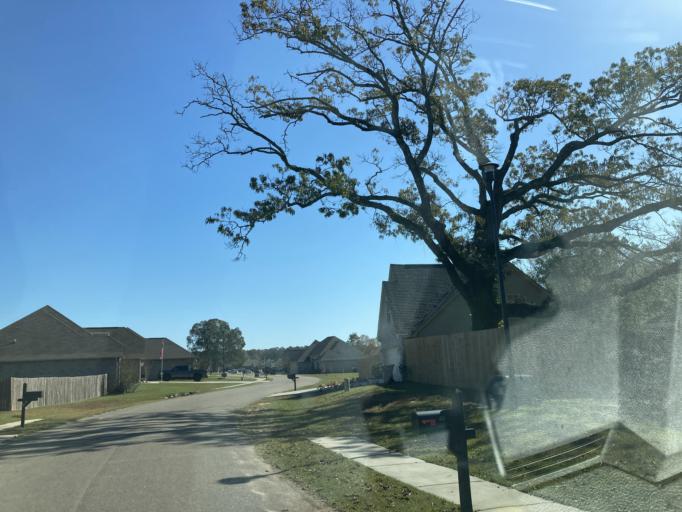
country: US
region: Mississippi
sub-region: Lamar County
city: West Hattiesburg
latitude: 31.2809
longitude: -89.4139
